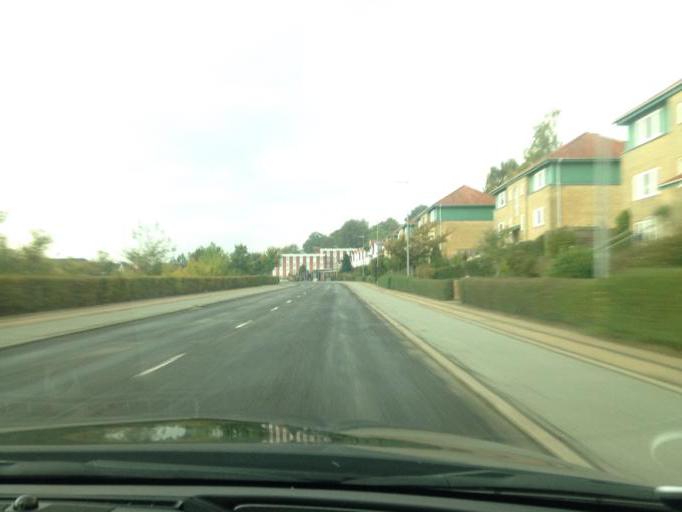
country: DK
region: South Denmark
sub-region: Kolding Kommune
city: Kolding
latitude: 55.4961
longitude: 9.4688
